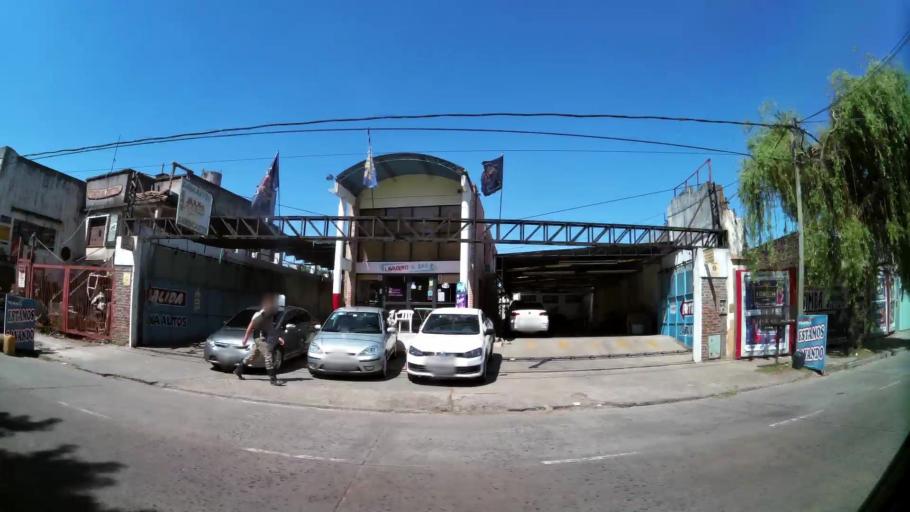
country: AR
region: Buenos Aires
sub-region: Partido de Tigre
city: Tigre
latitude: -34.4295
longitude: -58.5650
